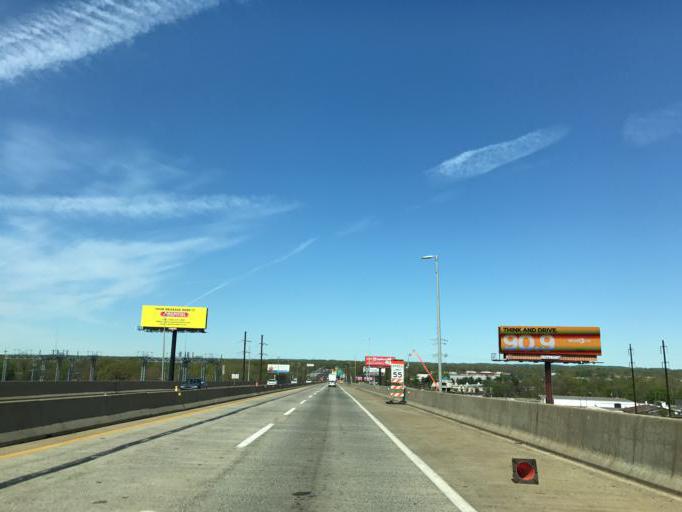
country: US
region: Pennsylvania
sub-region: Bucks County
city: Bristol
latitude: 40.1189
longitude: -74.8368
